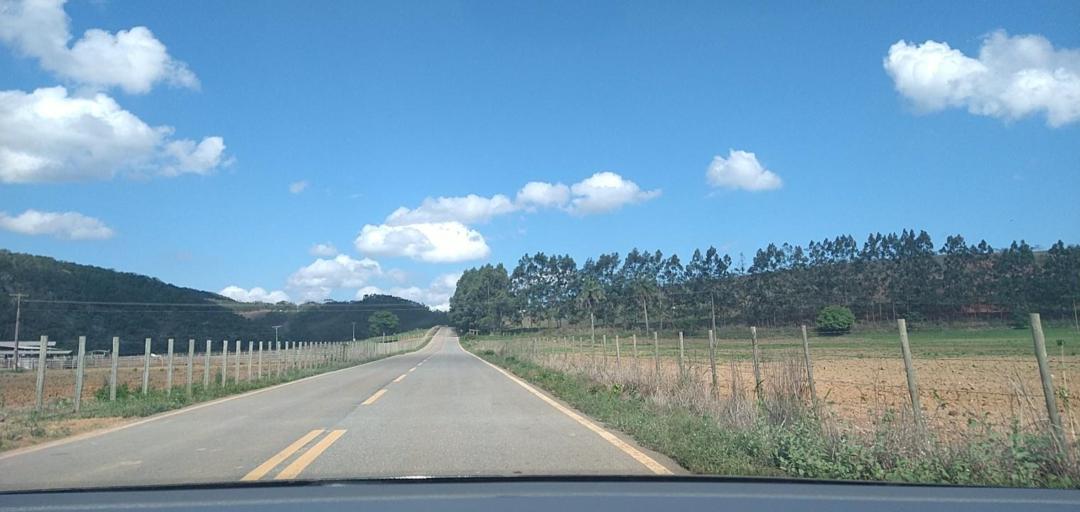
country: BR
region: Minas Gerais
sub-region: Alvinopolis
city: Alvinopolis
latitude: -20.0178
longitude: -43.0754
